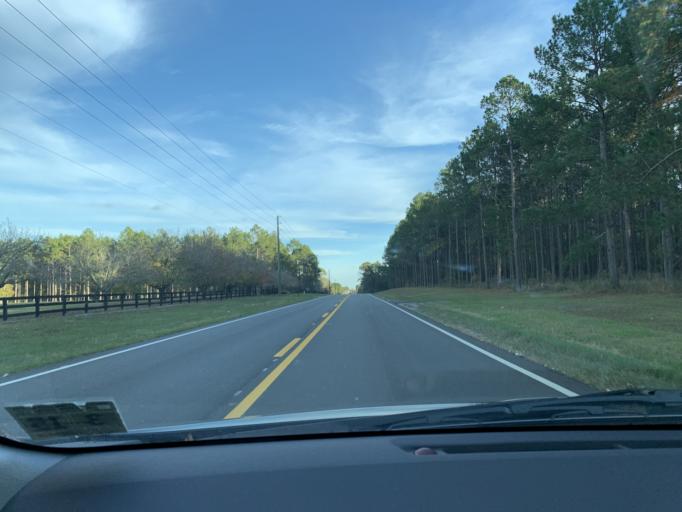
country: US
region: Georgia
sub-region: Irwin County
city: Ocilla
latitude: 31.5829
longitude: -83.0695
